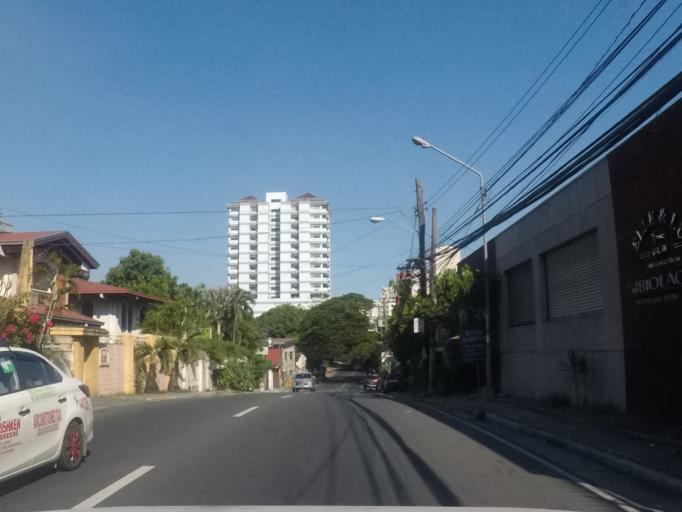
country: PH
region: Metro Manila
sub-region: San Juan
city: San Juan
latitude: 14.6076
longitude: 121.0330
